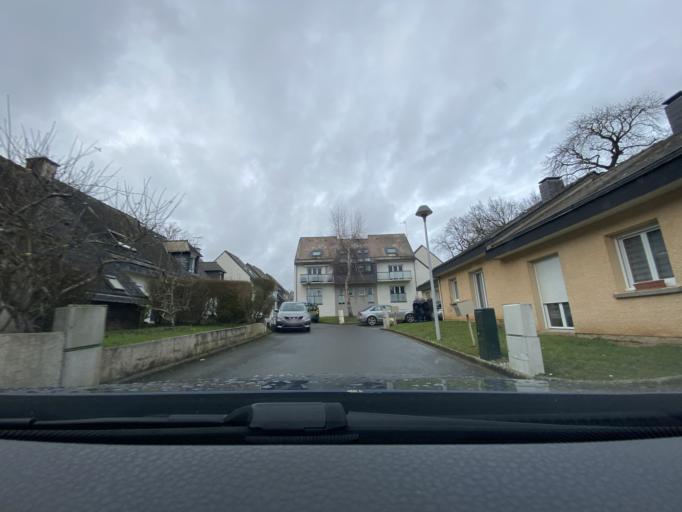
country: FR
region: Brittany
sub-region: Departement d'Ille-et-Vilaine
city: Melesse
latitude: 48.2187
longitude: -1.6949
